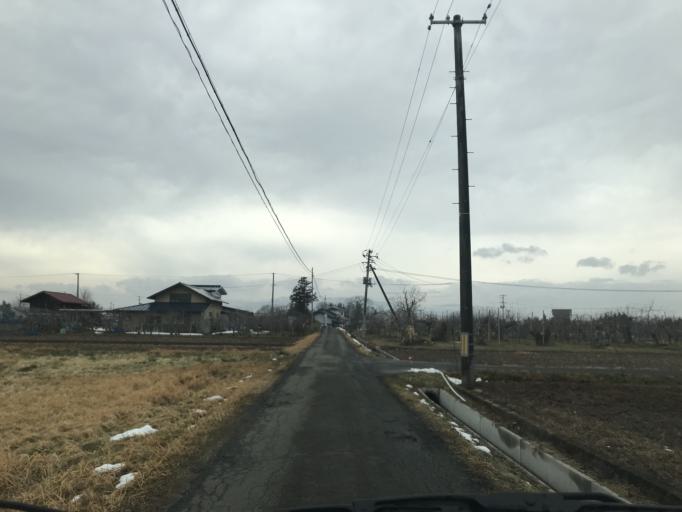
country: JP
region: Iwate
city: Mizusawa
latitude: 39.1837
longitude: 141.1326
